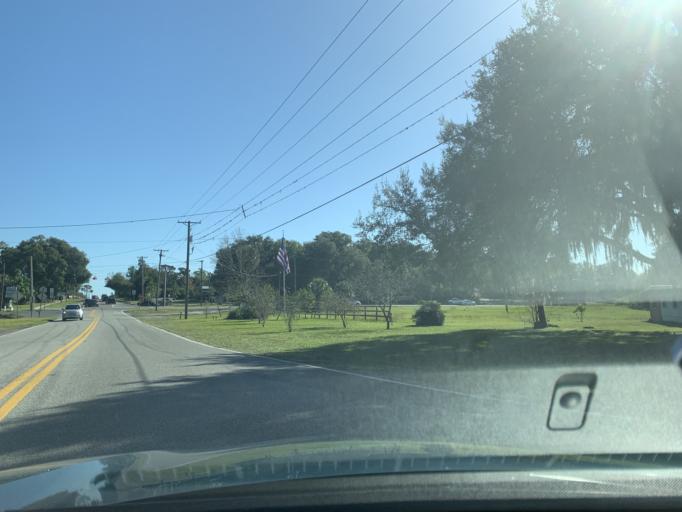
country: US
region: Florida
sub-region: Pasco County
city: San Antonio
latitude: 28.3356
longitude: -82.2715
